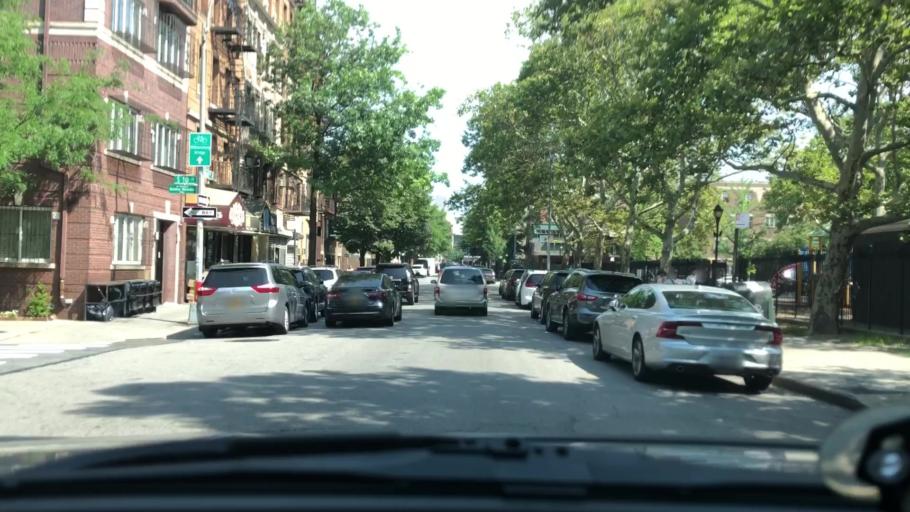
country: US
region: New York
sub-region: Queens County
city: Long Island City
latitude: 40.7079
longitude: -73.9644
